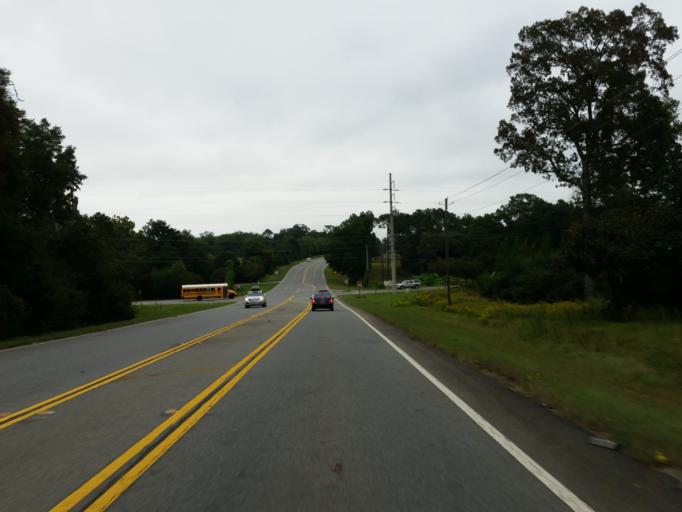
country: US
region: Georgia
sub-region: Houston County
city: Perry
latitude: 32.4810
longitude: -83.7604
